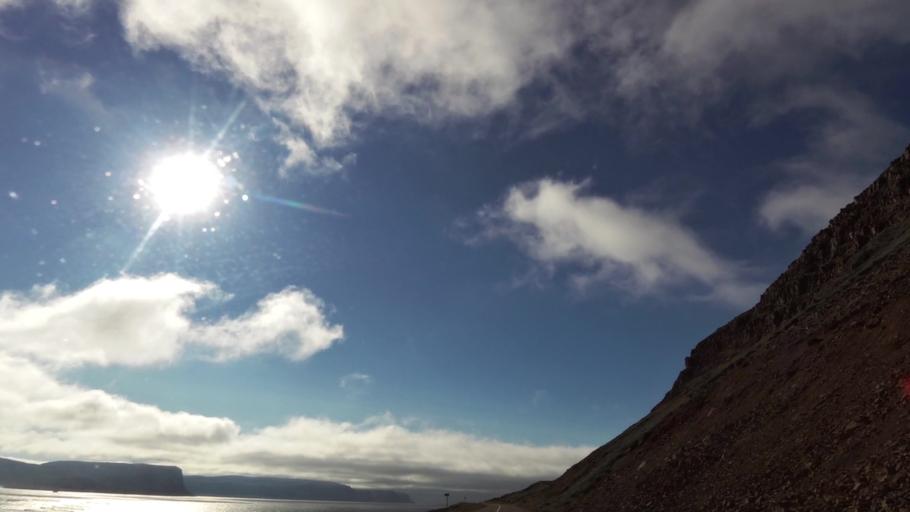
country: IS
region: West
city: Olafsvik
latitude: 65.5803
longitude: -23.9536
